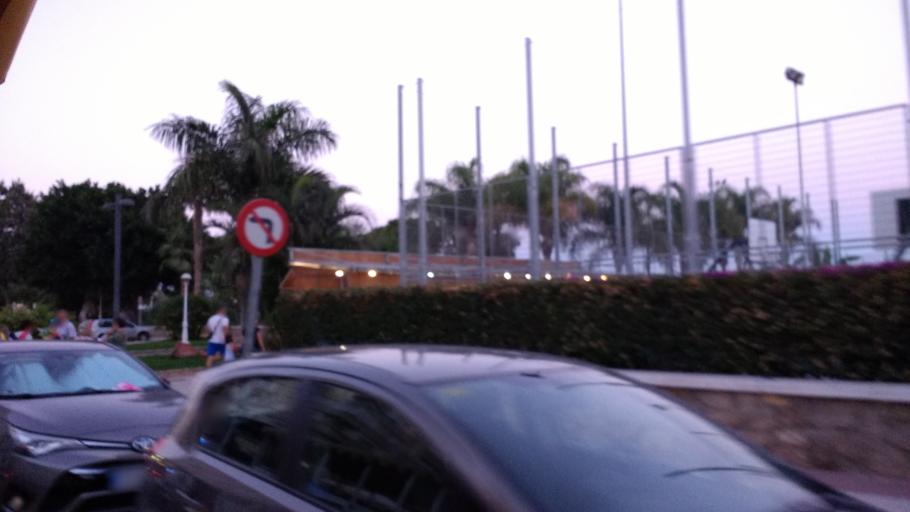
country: ES
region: Andalusia
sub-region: Provincia de Malaga
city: Velez-Malaga
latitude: 36.7363
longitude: -4.0956
